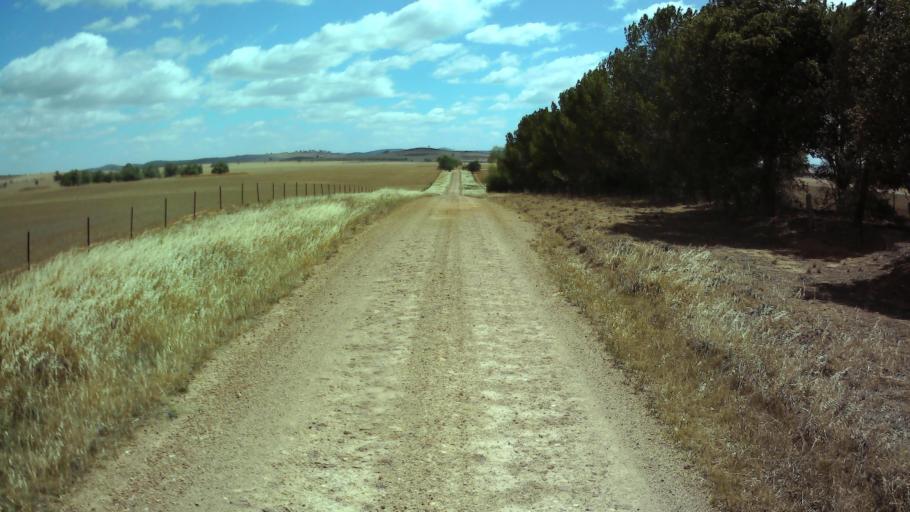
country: AU
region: New South Wales
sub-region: Weddin
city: Grenfell
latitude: -33.9942
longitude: 148.3143
